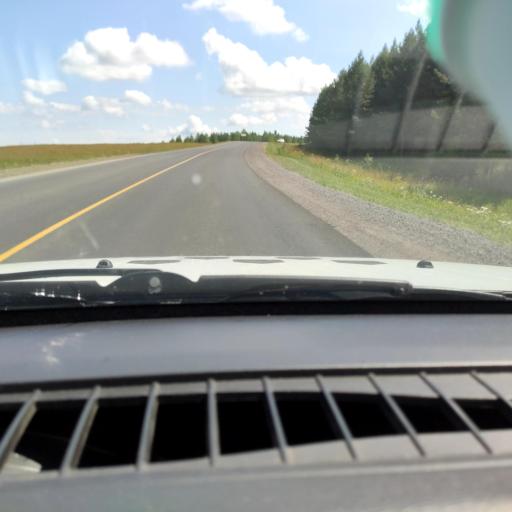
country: RU
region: Bashkortostan
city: Verkhniye Kigi
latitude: 55.3187
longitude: 58.7265
